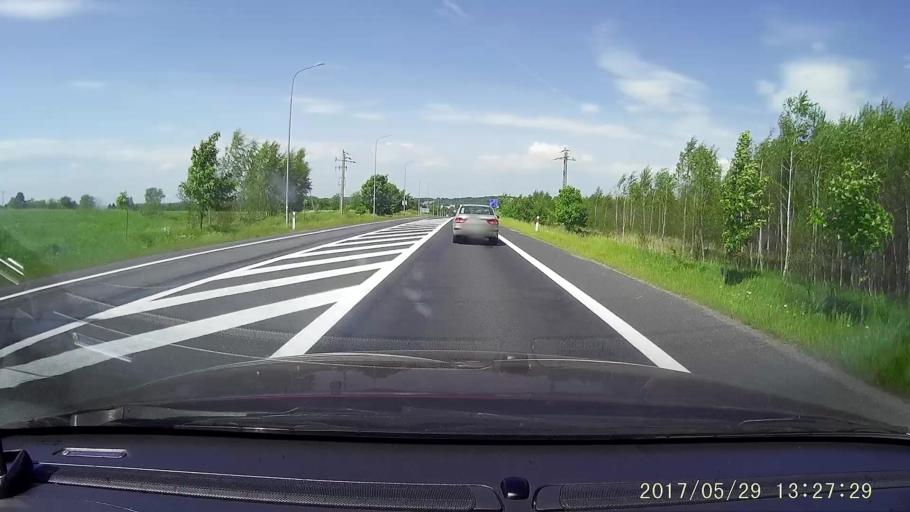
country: PL
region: Lower Silesian Voivodeship
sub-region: Powiat lubanski
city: Olszyna
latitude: 51.0554
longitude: 15.3733
